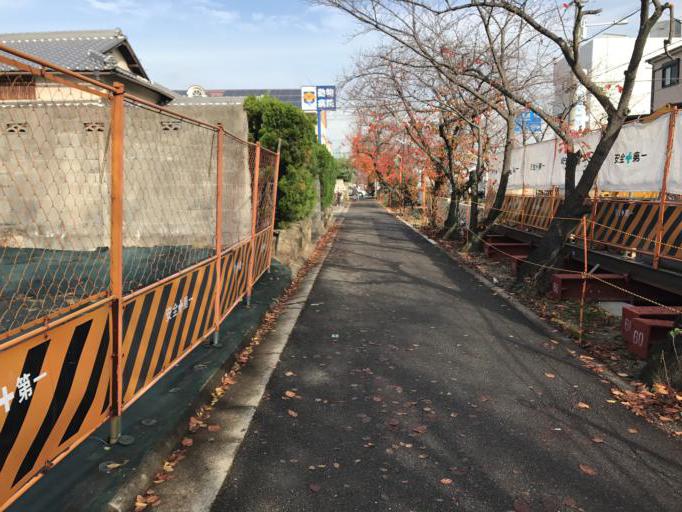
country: JP
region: Osaka
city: Yao
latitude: 34.6181
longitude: 135.6226
